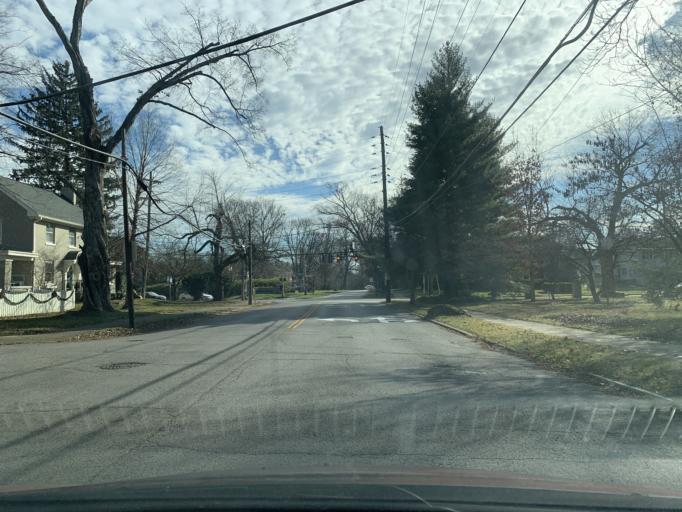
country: US
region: Kentucky
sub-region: Jefferson County
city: Saint Matthews
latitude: 38.2492
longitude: -85.6810
